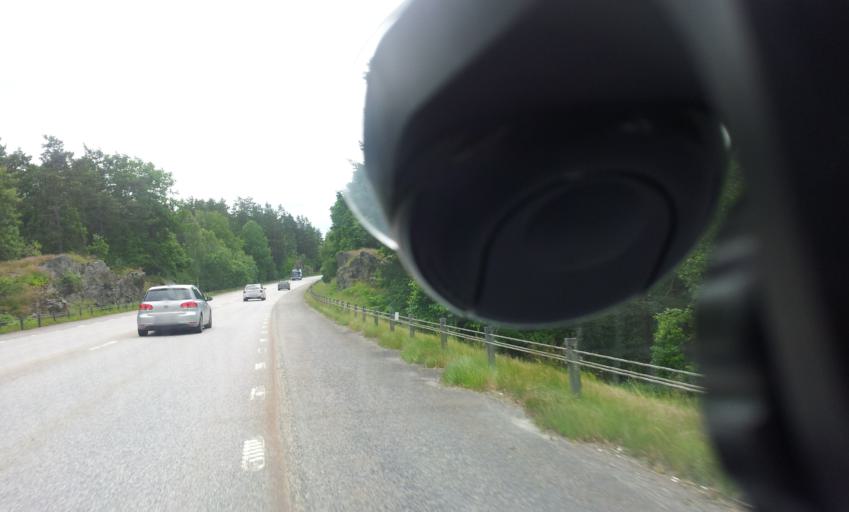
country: SE
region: Kalmar
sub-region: Vasterviks Kommun
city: Ankarsrum
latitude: 57.6802
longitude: 16.4434
